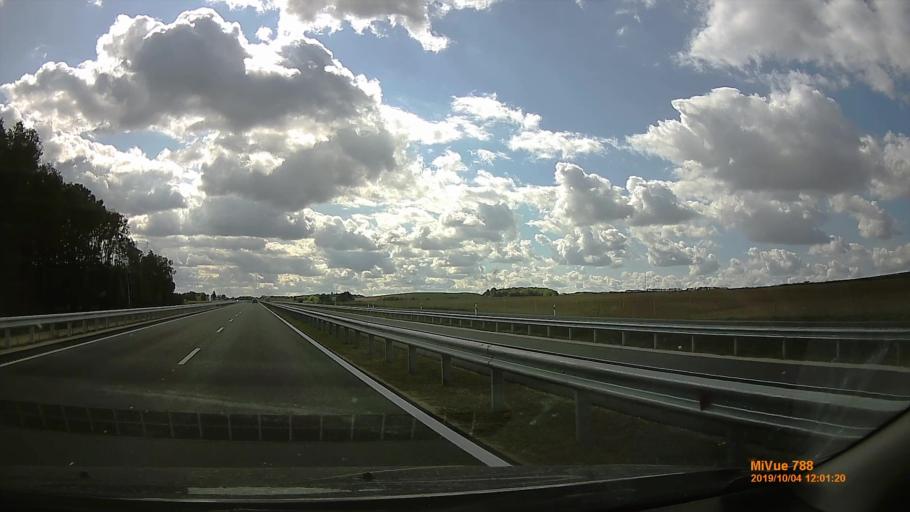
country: HU
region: Somogy
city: Karad
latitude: 46.6138
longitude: 17.7974
